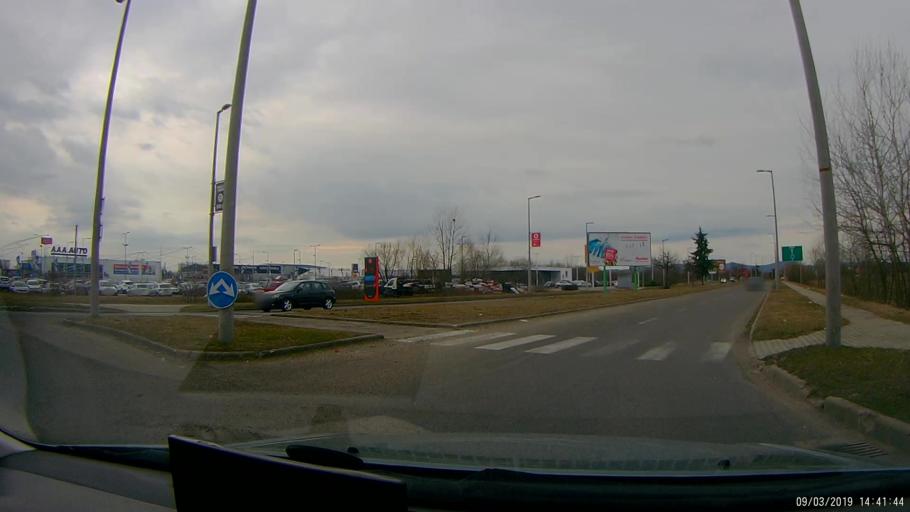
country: HU
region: Budapest
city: Budapest XV. keruelet
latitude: 47.5809
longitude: 19.1590
